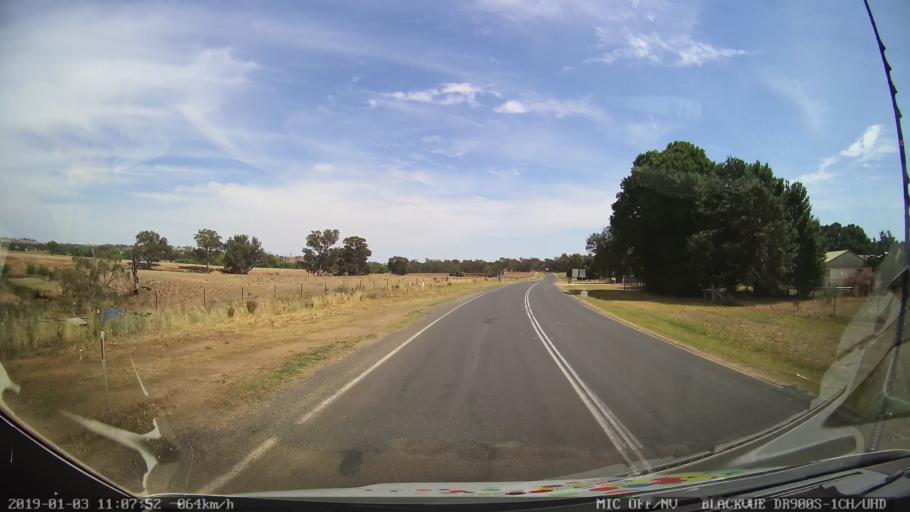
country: AU
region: New South Wales
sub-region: Young
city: Young
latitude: -34.2553
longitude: 148.2591
